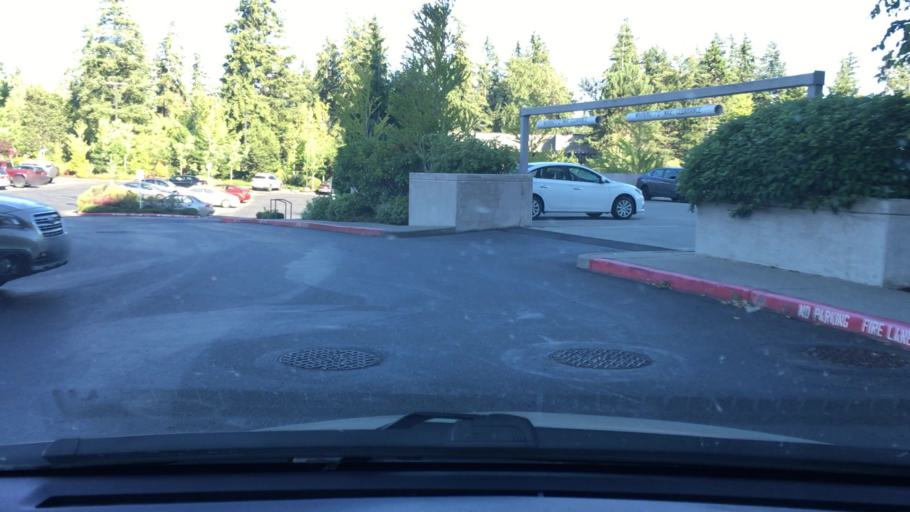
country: US
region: Washington
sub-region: King County
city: Eastgate
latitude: 47.5836
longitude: -122.1294
